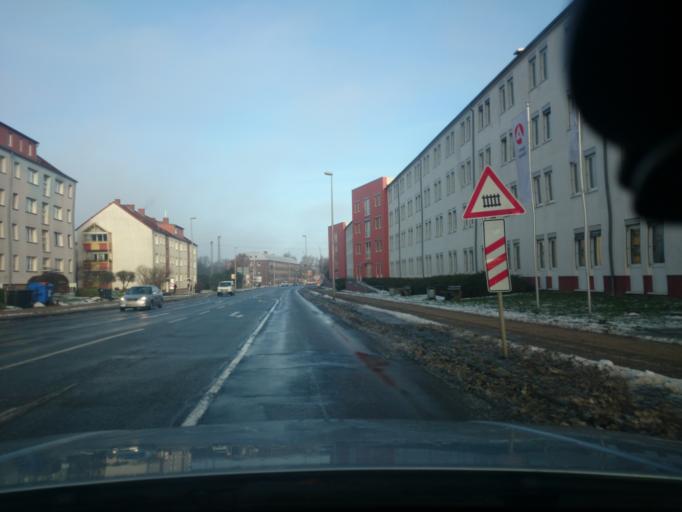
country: DE
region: Mecklenburg-Vorpommern
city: Stralsund
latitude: 54.3073
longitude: 13.0688
